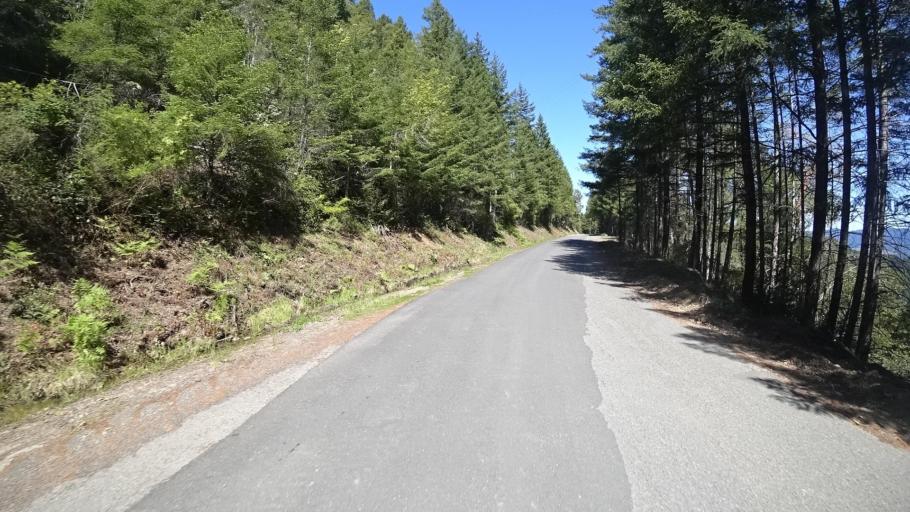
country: US
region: California
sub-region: Humboldt County
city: Redway
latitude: 40.1509
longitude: -124.0643
